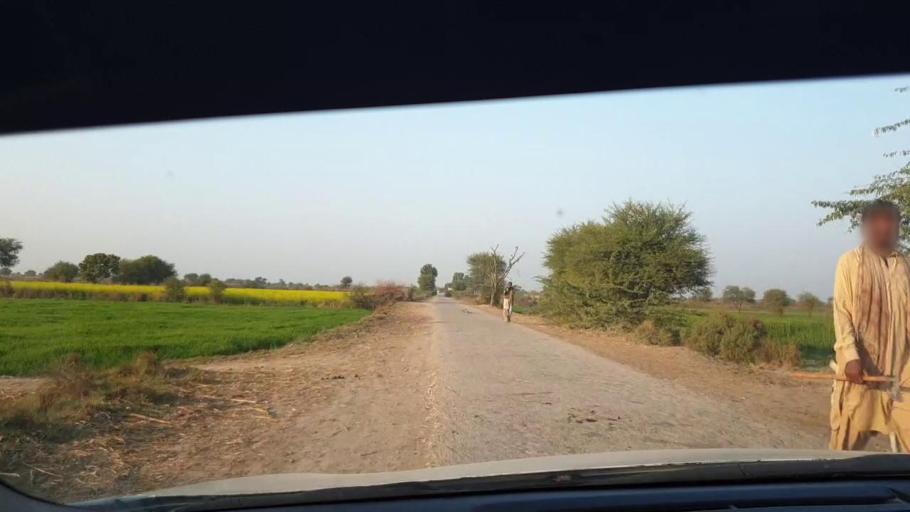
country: PK
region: Sindh
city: Berani
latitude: 25.8554
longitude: 68.8165
